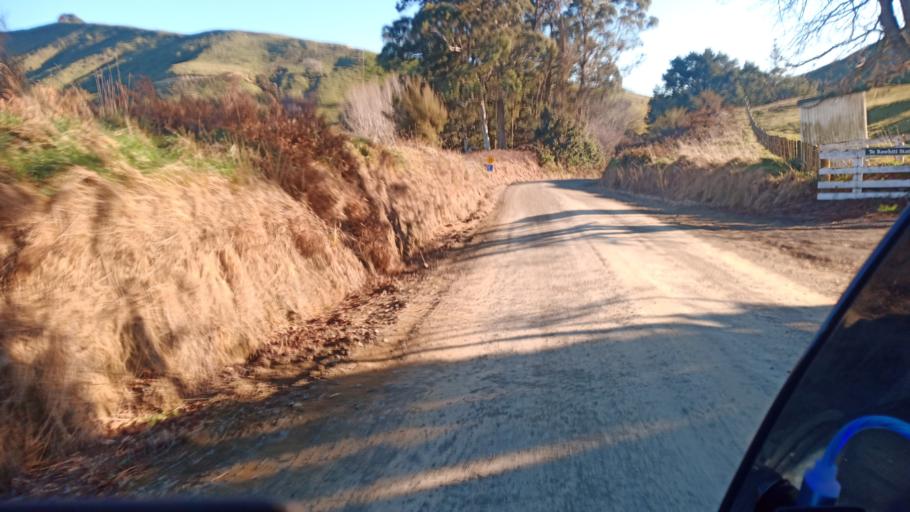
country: NZ
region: Bay of Plenty
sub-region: Opotiki District
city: Opotiki
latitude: -38.4602
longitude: 177.4250
